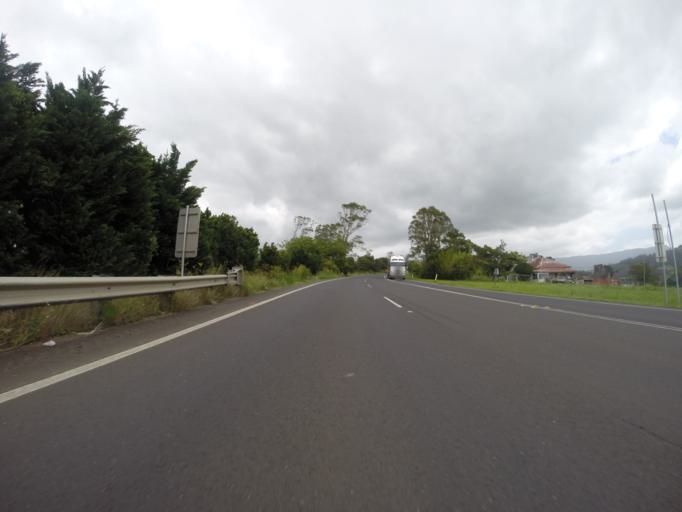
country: AU
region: New South Wales
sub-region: Kiama
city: Gerringong
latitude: -34.7510
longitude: 150.7822
